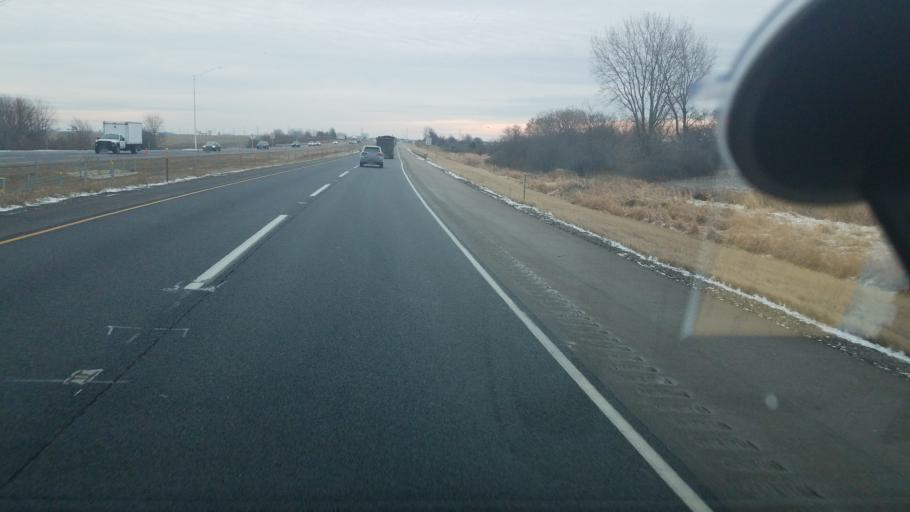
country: US
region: Illinois
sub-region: Kane County
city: Sugar Grove
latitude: 41.8166
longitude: -88.4567
